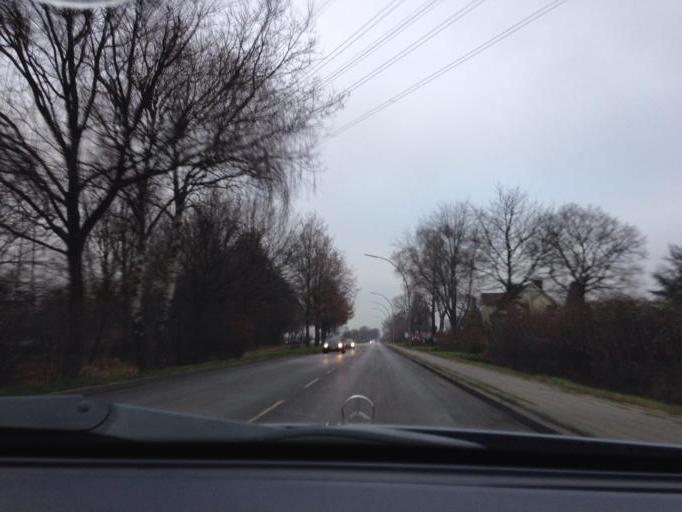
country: DE
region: Schleswig-Holstein
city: Stapelfeld
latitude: 53.6337
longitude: 10.1864
